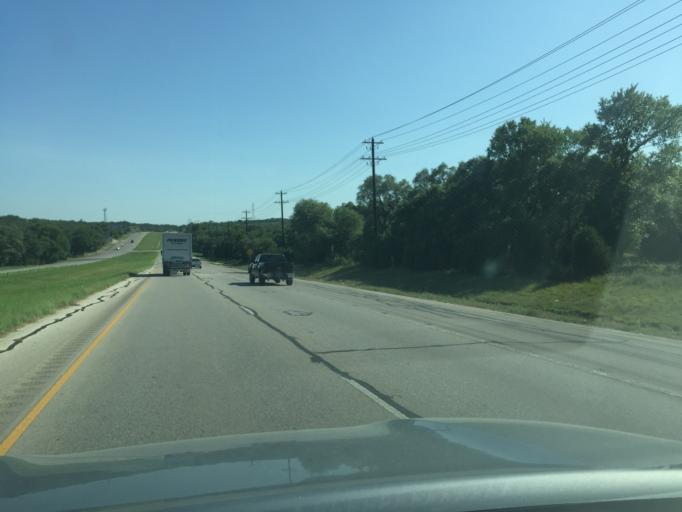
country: US
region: Texas
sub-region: Comal County
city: Bulverde
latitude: 29.7890
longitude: -98.4220
